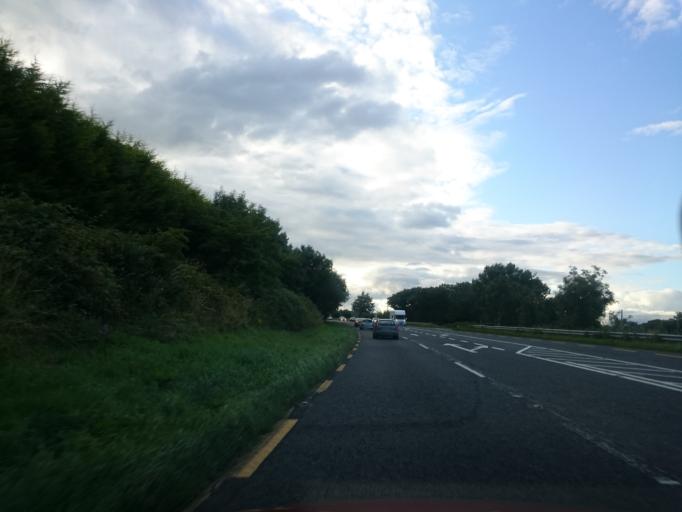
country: IE
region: Leinster
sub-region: Loch Garman
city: Loch Garman
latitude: 52.3593
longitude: -6.5076
